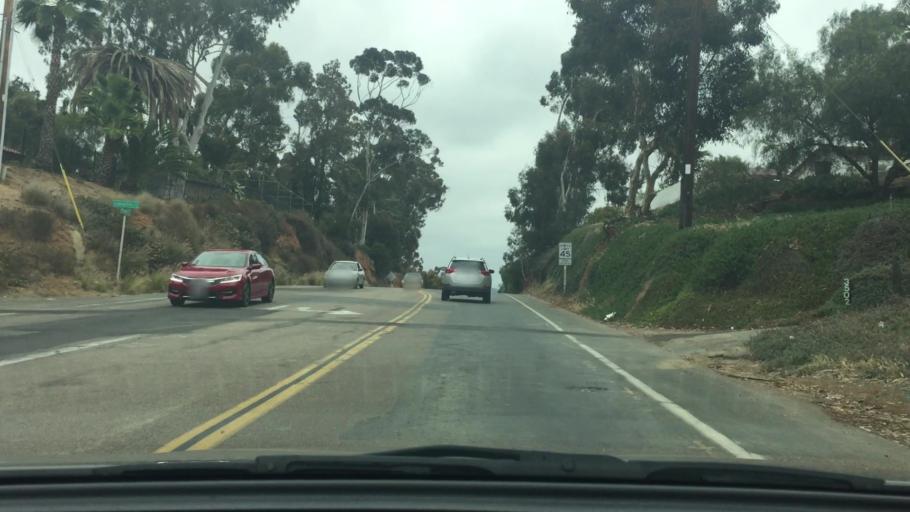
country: US
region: California
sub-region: San Diego County
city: Bonita
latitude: 32.6597
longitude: -117.0534
